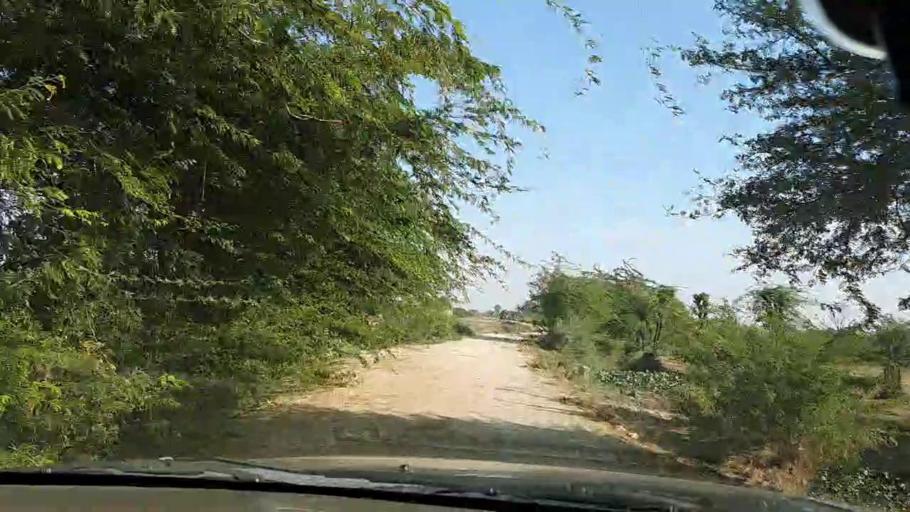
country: PK
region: Sindh
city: Mirpur Batoro
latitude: 24.6288
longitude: 68.2689
